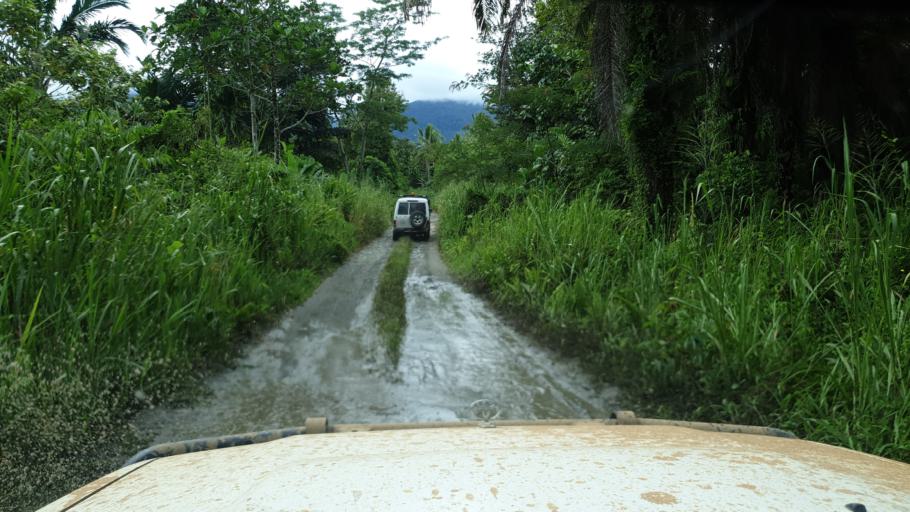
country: PG
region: Northern Province
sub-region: Sohe
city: Kokoda
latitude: -8.9302
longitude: 147.8684
